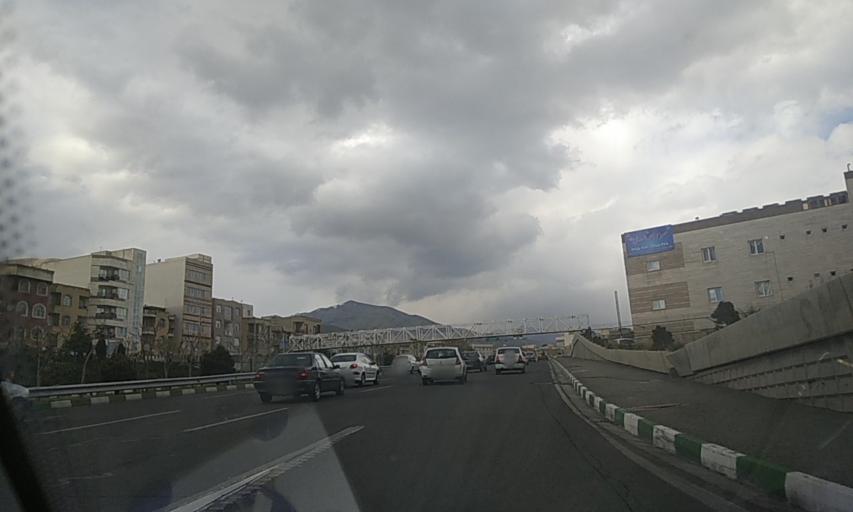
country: IR
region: Tehran
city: Tajrish
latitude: 35.7715
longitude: 51.3191
